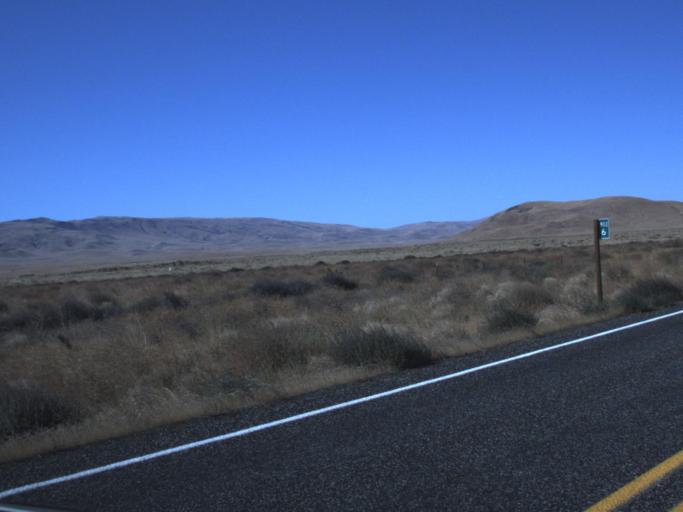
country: US
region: Washington
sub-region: Benton County
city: Benton City
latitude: 46.5101
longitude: -119.6557
